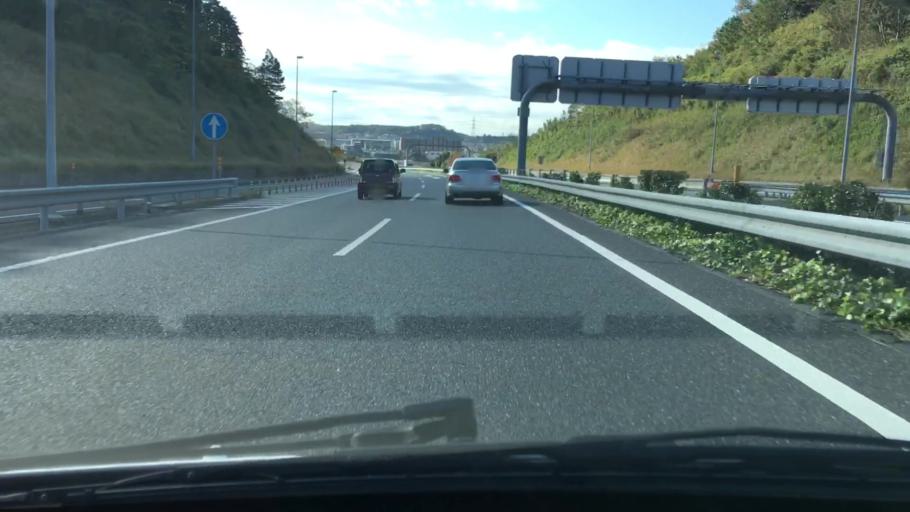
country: JP
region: Chiba
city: Kisarazu
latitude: 35.3528
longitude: 139.9473
